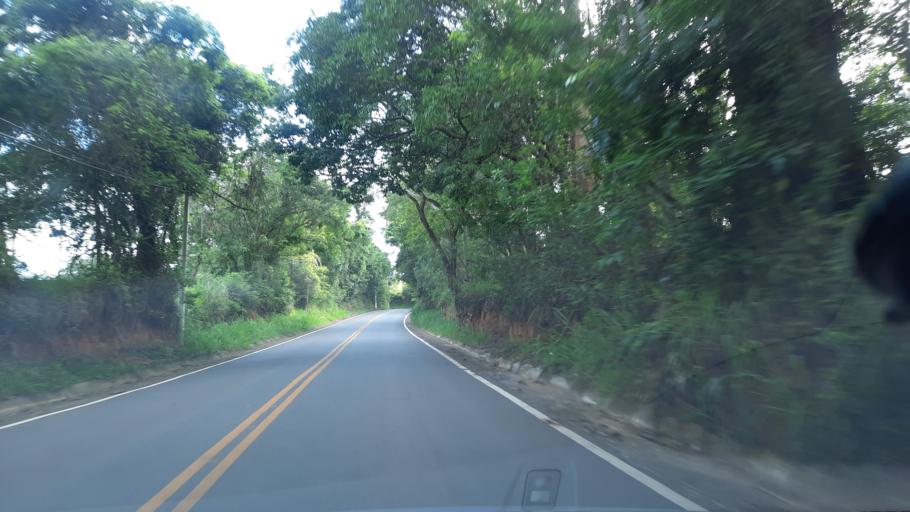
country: BR
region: Sao Paulo
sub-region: Atibaia
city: Atibaia
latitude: -23.0981
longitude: -46.5176
